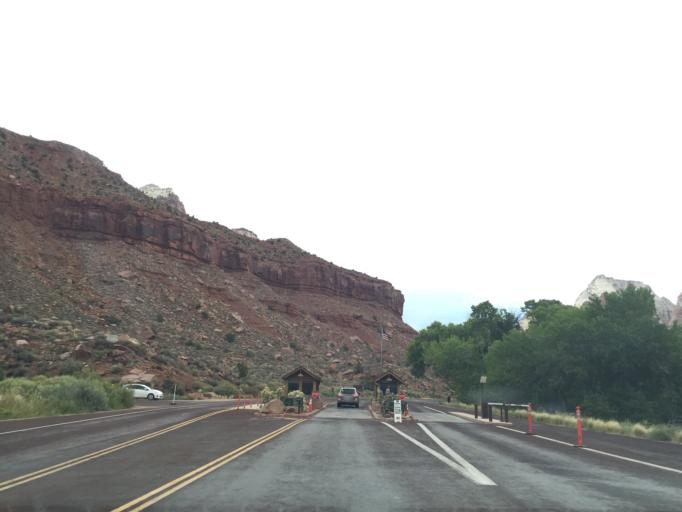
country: US
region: Utah
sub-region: Washington County
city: Hildale
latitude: 37.2016
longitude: -112.9886
